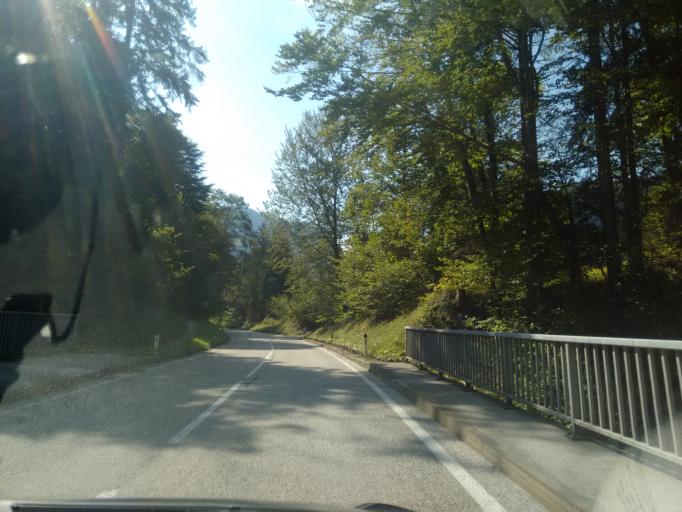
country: AT
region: Upper Austria
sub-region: Politischer Bezirk Gmunden
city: Gruenau im Almtal
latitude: 47.7854
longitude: 13.9593
